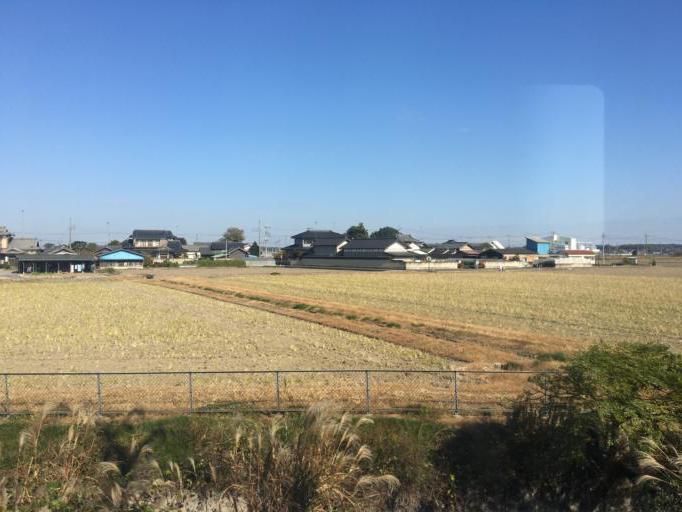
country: JP
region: Tochigi
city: Oyama
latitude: 36.3479
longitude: 139.7872
